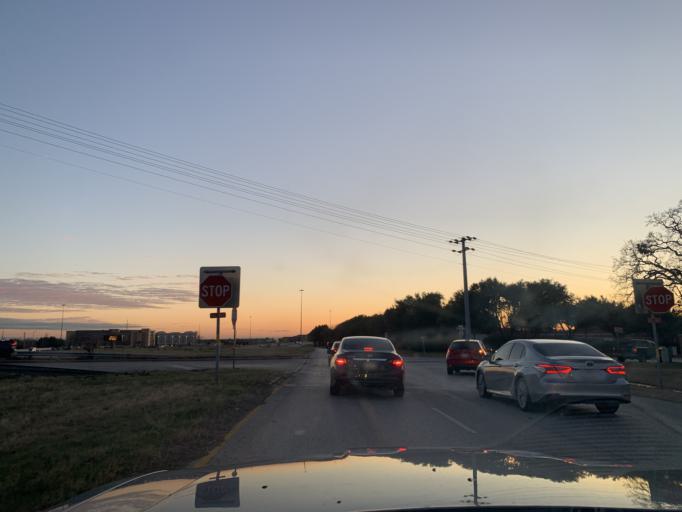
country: US
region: Texas
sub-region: Tarrant County
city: Bedford
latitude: 32.8450
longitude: -97.1168
